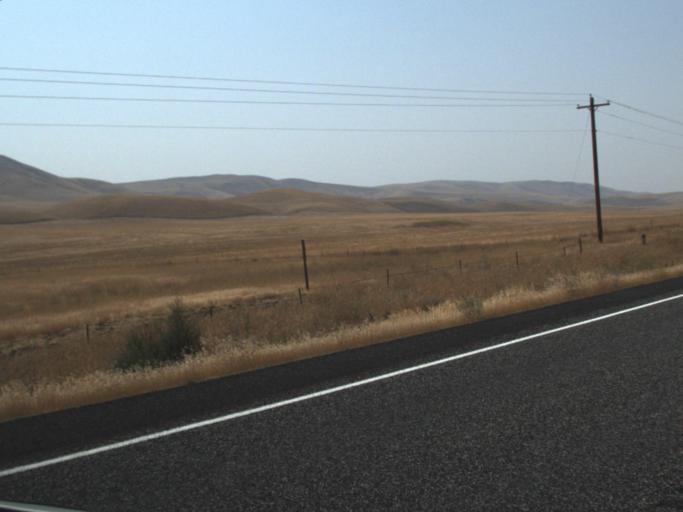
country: US
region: Washington
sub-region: Grant County
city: Desert Aire
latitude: 46.5195
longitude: -119.9794
